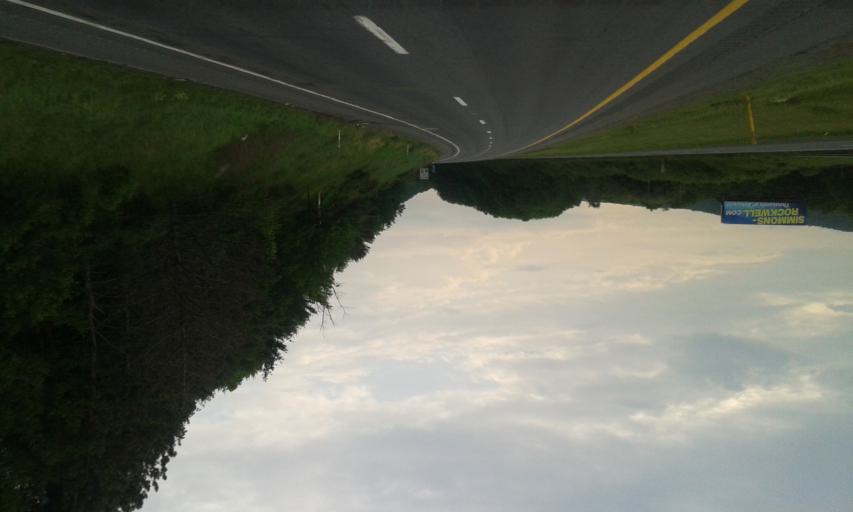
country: US
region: Pennsylvania
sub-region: Susquehanna County
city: Hallstead
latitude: 41.8736
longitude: -75.7204
